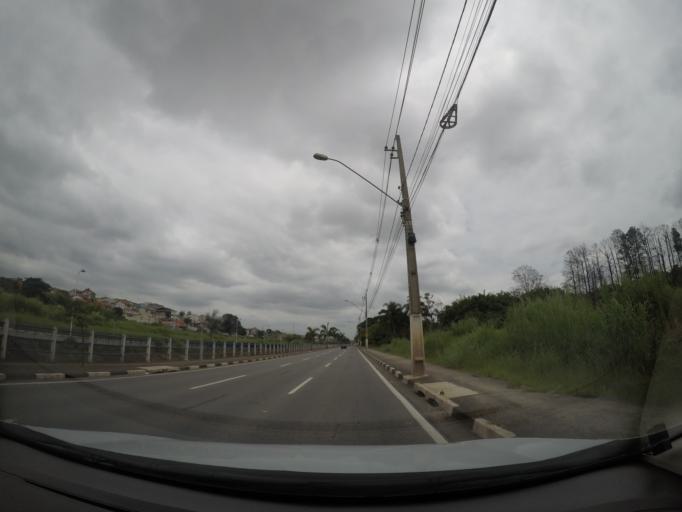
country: BR
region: Sao Paulo
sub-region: Aruja
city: Aruja
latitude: -23.3989
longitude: -46.3399
